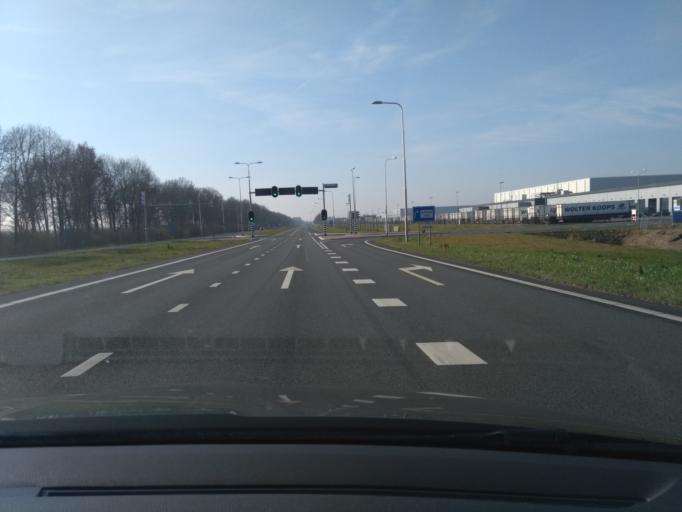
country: NL
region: Flevoland
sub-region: Gemeente Zeewolde
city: Zeewolde
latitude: 52.3620
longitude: 5.5232
